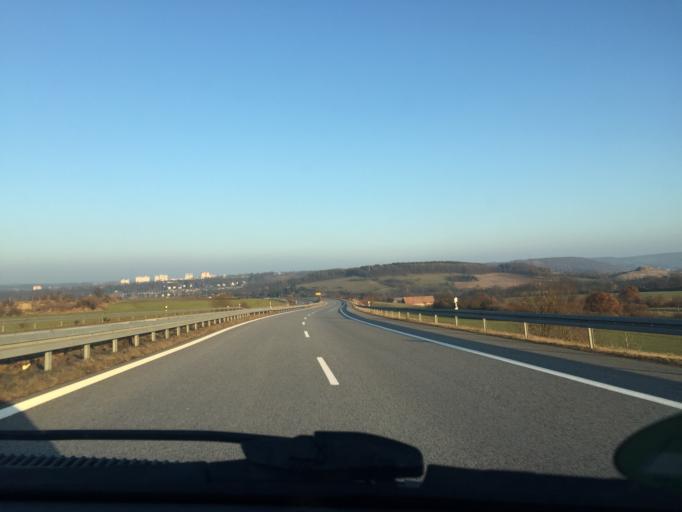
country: DE
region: Saxony
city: Pirna
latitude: 50.9472
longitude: 13.9117
